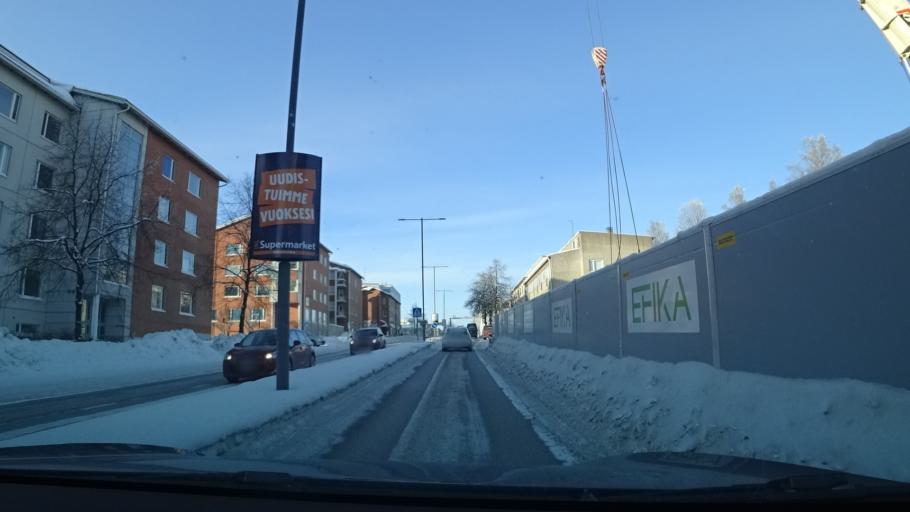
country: FI
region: South Karelia
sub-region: Lappeenranta
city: Lappeenranta
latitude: 61.0530
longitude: 28.1920
